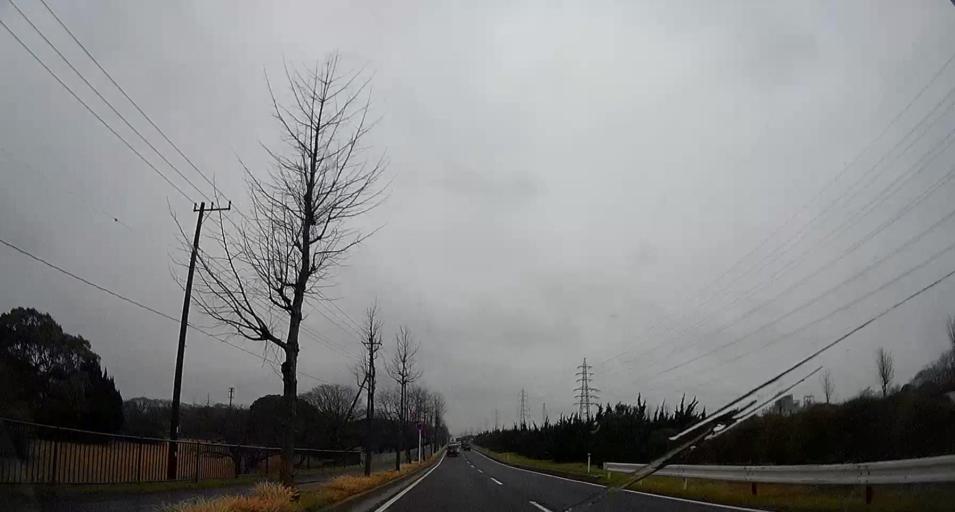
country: JP
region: Chiba
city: Ichihara
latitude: 35.5049
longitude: 140.0522
